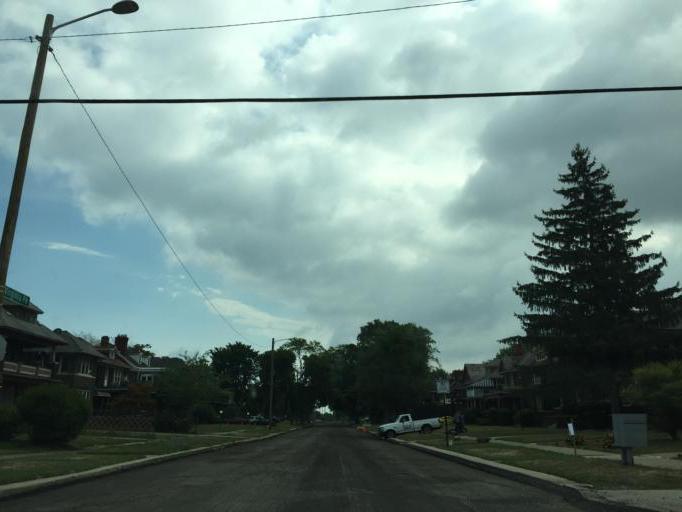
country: US
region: Michigan
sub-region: Wayne County
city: Highland Park
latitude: 42.3708
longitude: -83.0922
